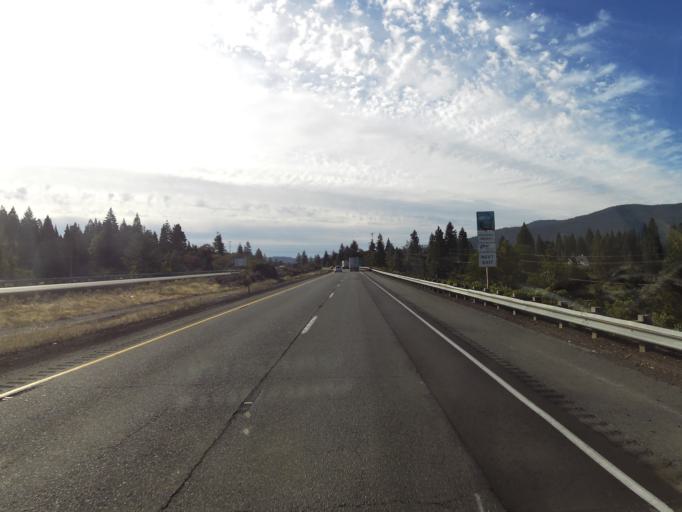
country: US
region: California
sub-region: Siskiyou County
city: Mount Shasta
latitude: 41.2920
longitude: -122.3102
